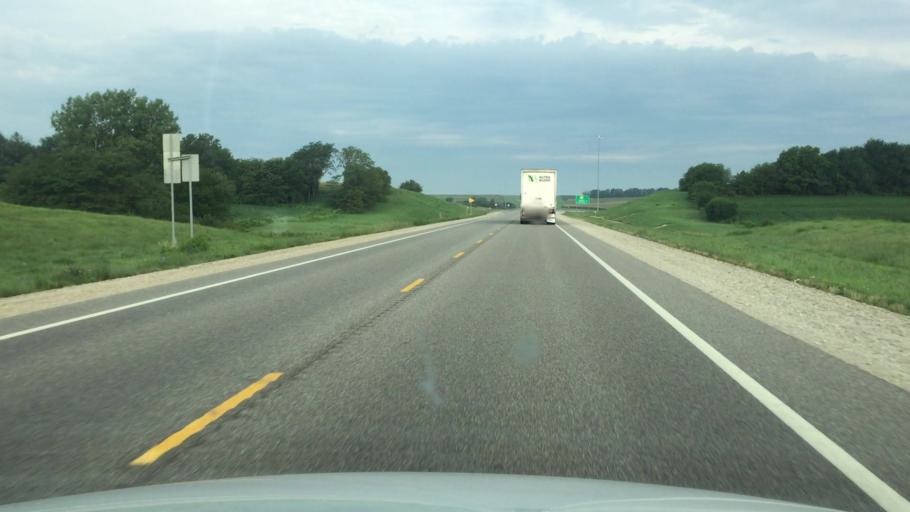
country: US
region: Kansas
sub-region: Doniphan County
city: Highland
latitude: 39.8385
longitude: -95.2574
